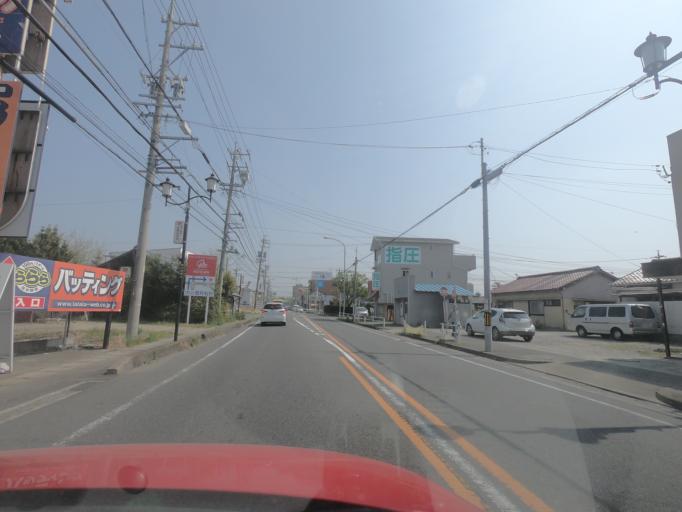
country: JP
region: Aichi
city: Kasugai
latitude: 35.2539
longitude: 136.9864
